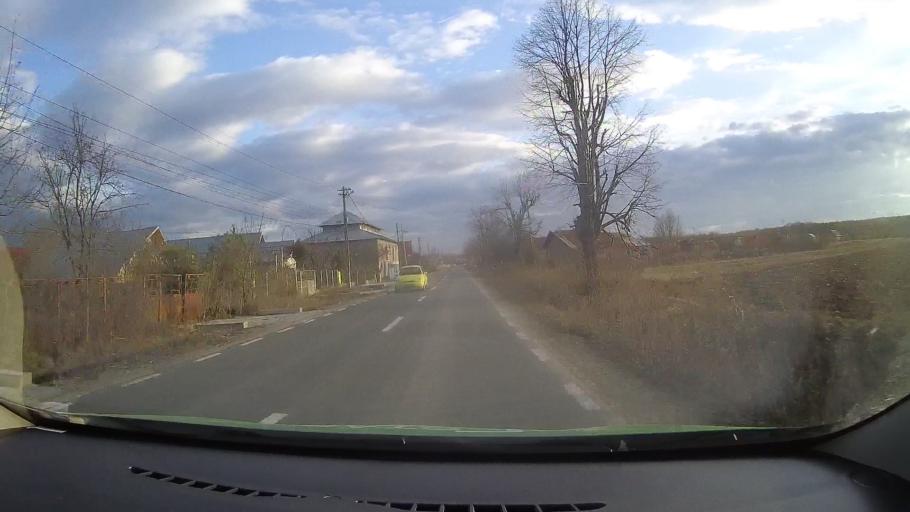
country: RO
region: Dambovita
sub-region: Comuna I. L. Caragiale
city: Ghirdoveni
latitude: 44.9565
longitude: 25.6576
